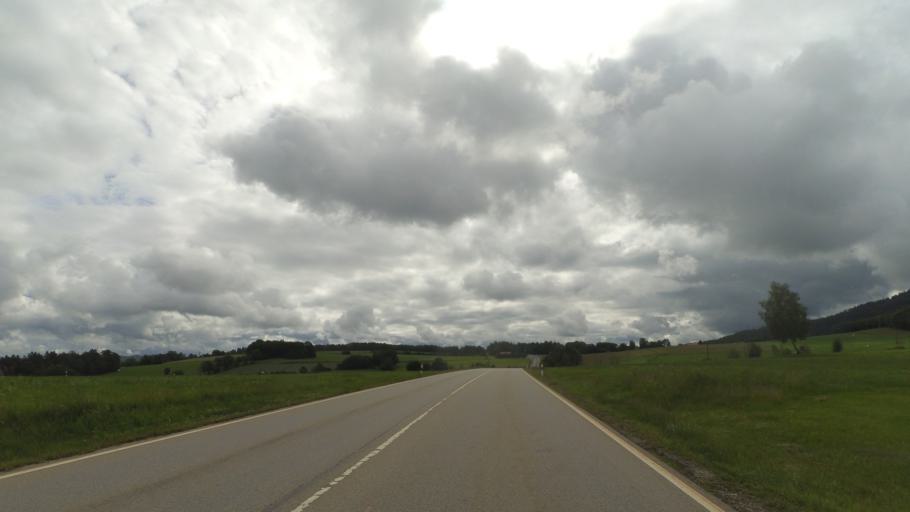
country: DE
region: Bavaria
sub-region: Lower Bavaria
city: Prackenbach
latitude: 49.0912
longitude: 12.8333
